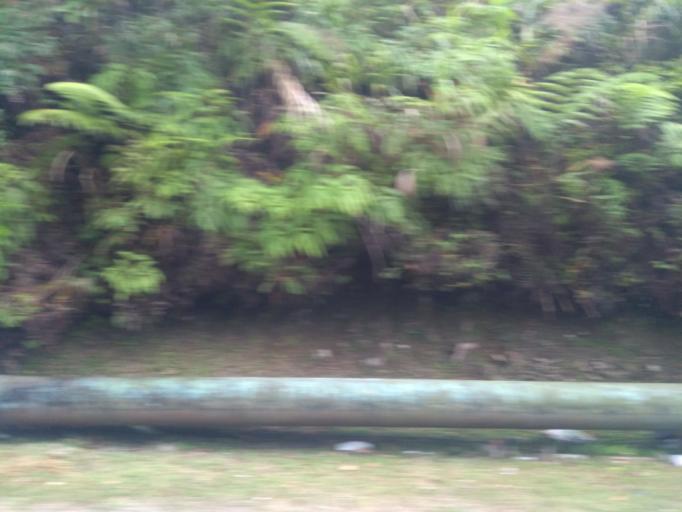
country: MY
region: Pahang
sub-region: Cameron Highlands
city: Tanah Rata
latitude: 4.5213
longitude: 101.4293
